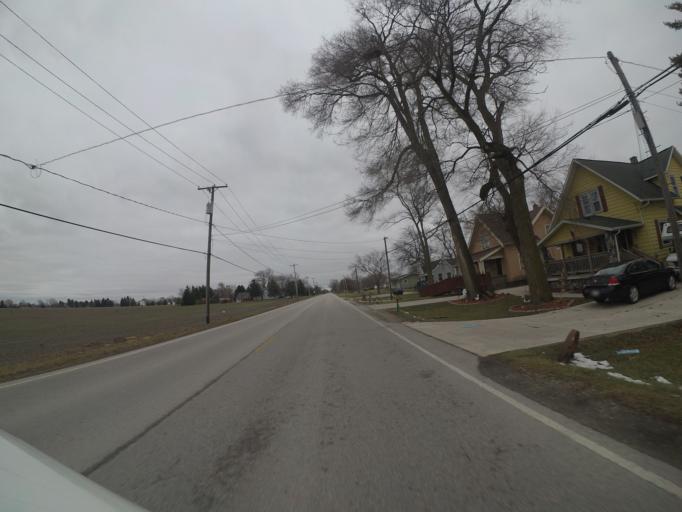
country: US
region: Ohio
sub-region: Wood County
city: Walbridge
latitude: 41.5755
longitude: -83.5122
